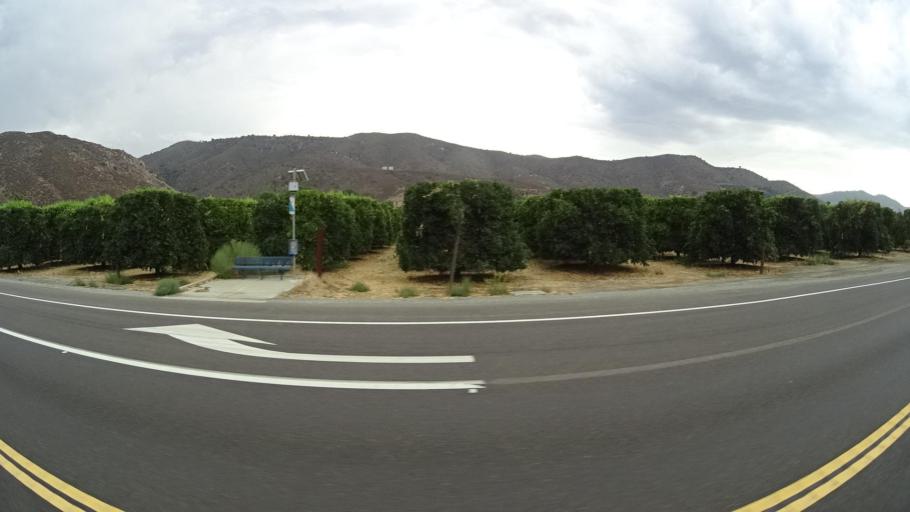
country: US
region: California
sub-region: San Diego County
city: San Pasqual
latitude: 33.0906
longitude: -116.9486
